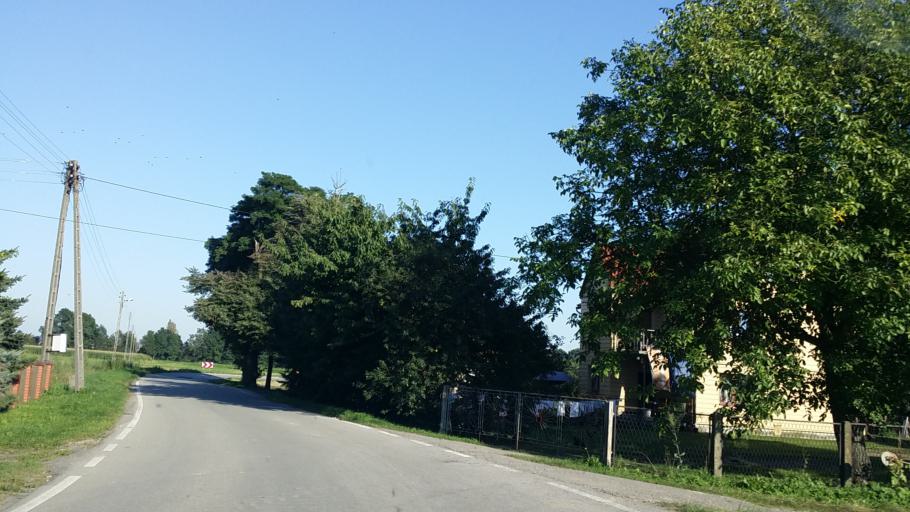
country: PL
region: Lesser Poland Voivodeship
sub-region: Powiat wadowicki
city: Spytkowice
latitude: 50.0226
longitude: 19.4882
